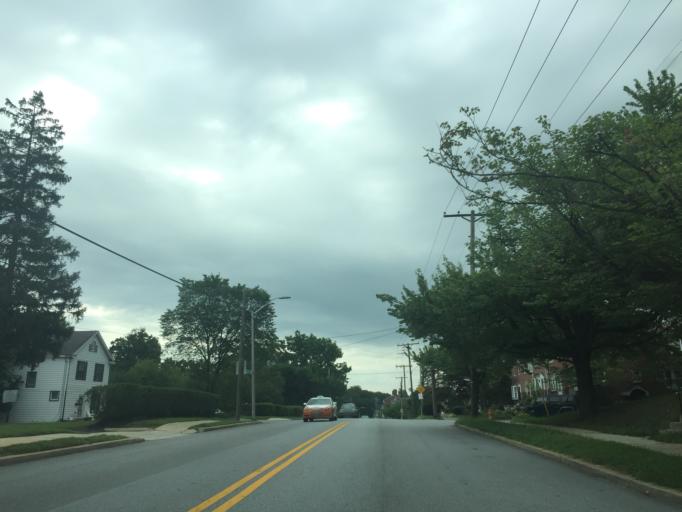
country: US
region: Maryland
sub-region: Baltimore County
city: Charlestown
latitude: 39.2965
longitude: -76.7073
